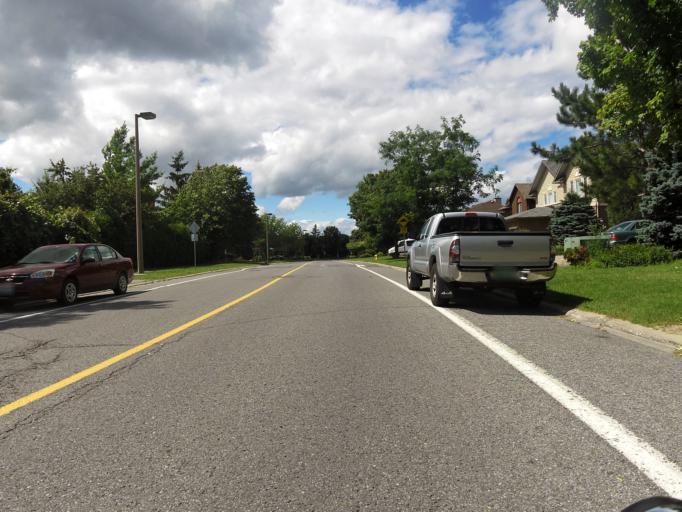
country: CA
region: Ontario
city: Bells Corners
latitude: 45.3227
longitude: -75.9076
